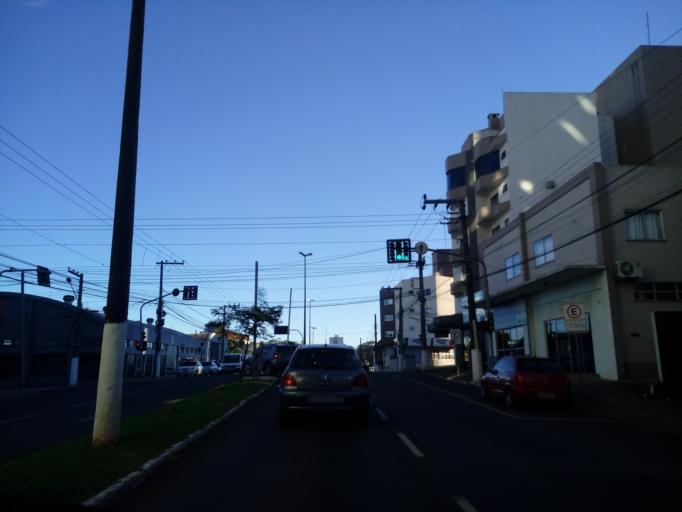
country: BR
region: Santa Catarina
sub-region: Chapeco
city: Chapeco
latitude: -27.0919
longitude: -52.6157
